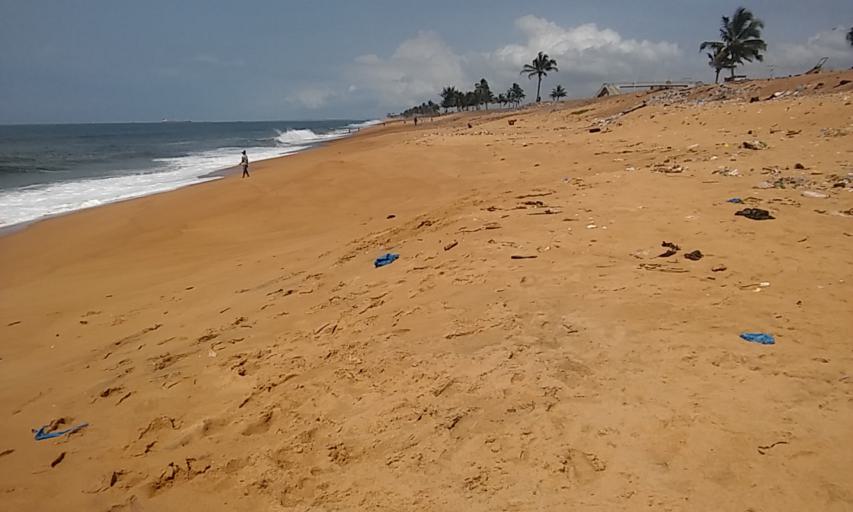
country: CI
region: Lagunes
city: Bingerville
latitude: 5.2389
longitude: -3.8995
